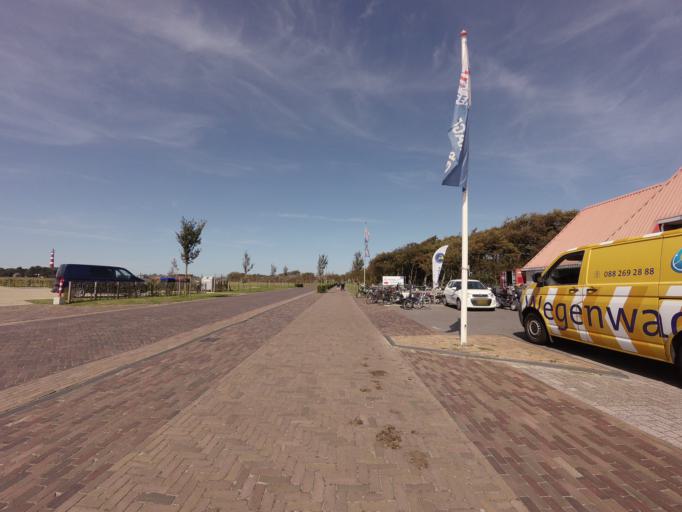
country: NL
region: Friesland
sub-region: Gemeente Ameland
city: Hollum
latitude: 53.4444
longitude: 5.6351
